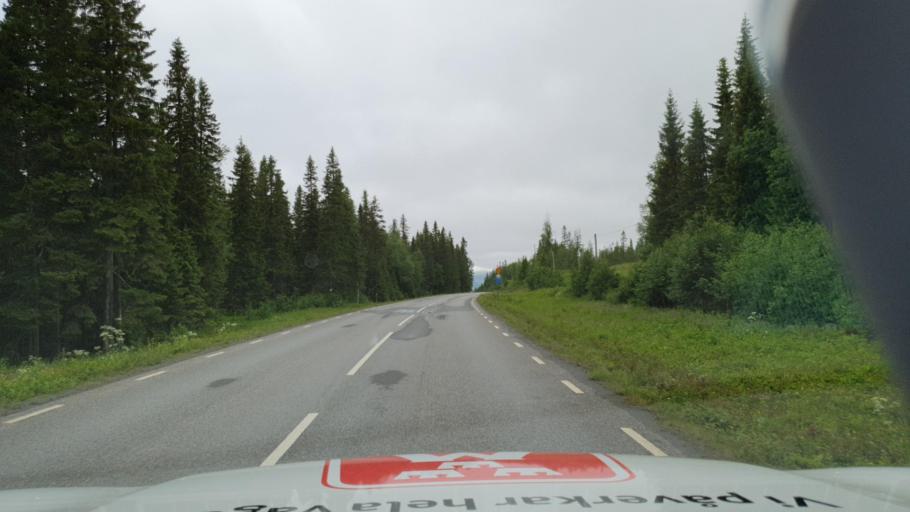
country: SE
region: Jaemtland
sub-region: Are Kommun
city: Are
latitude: 63.5310
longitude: 13.0757
